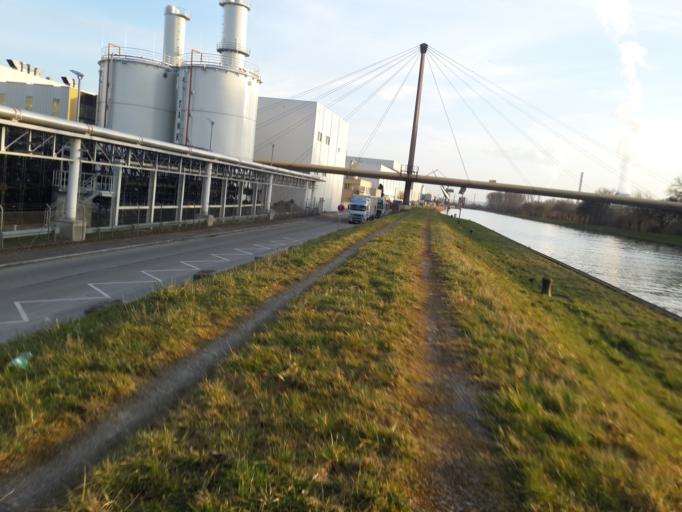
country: DE
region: Baden-Wuerttemberg
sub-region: Regierungsbezirk Stuttgart
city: Untereisesheim
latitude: 49.2053
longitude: 9.2176
